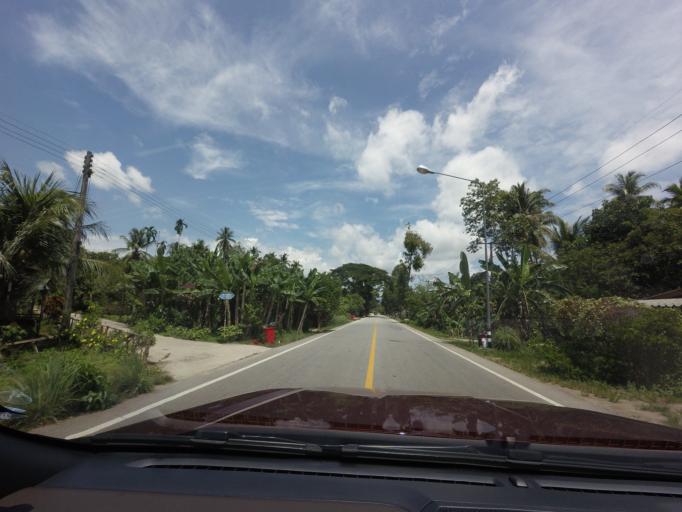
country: TH
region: Narathiwat
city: Ra-ngae
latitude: 6.2597
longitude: 101.6907
